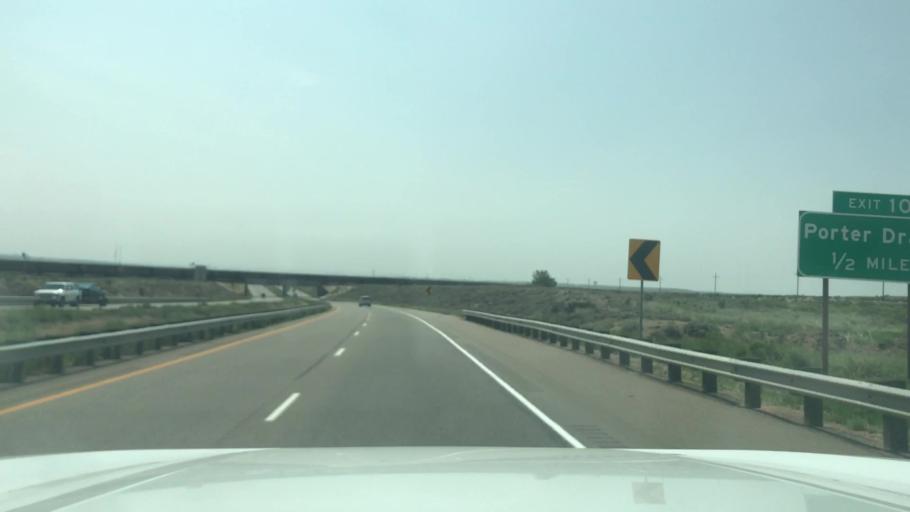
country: US
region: Colorado
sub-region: Pueblo County
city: Pueblo West
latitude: 38.3921
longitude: -104.6201
